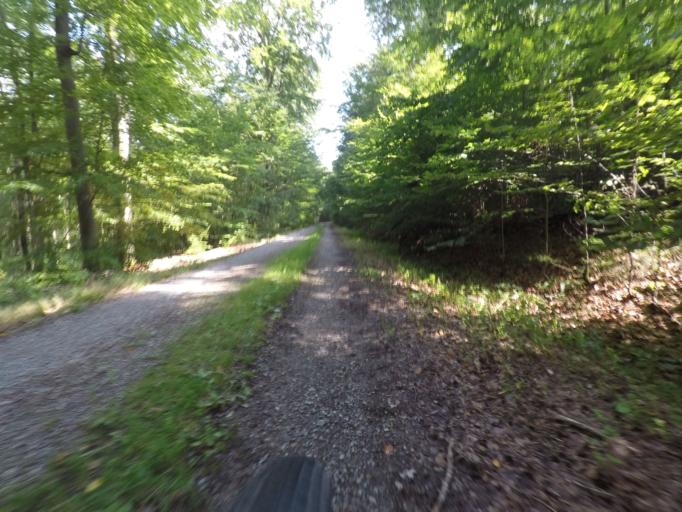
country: DE
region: Baden-Wuerttemberg
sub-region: Regierungsbezirk Stuttgart
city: Steinenbronn
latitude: 48.6776
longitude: 9.1077
